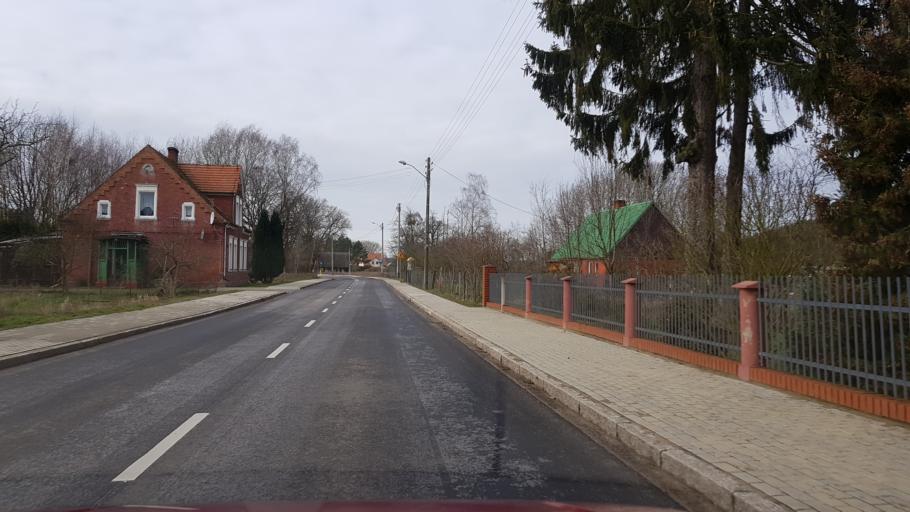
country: PL
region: West Pomeranian Voivodeship
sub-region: Powiat policki
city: Nowe Warpno
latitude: 53.6729
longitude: 14.3946
